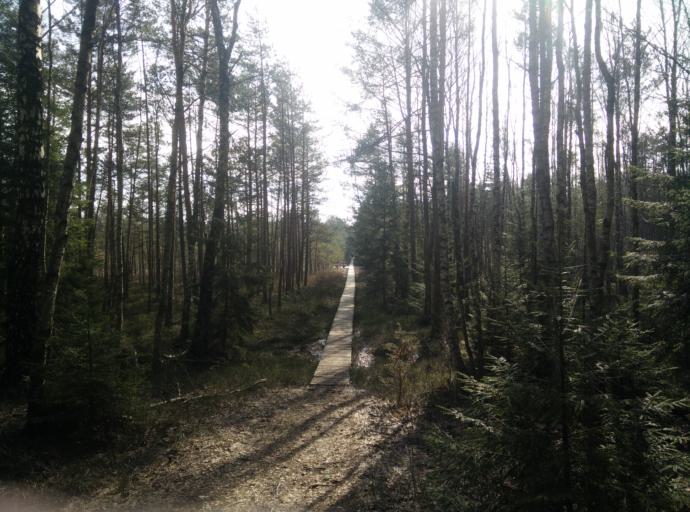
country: LT
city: Trakai
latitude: 54.6431
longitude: 24.9677
